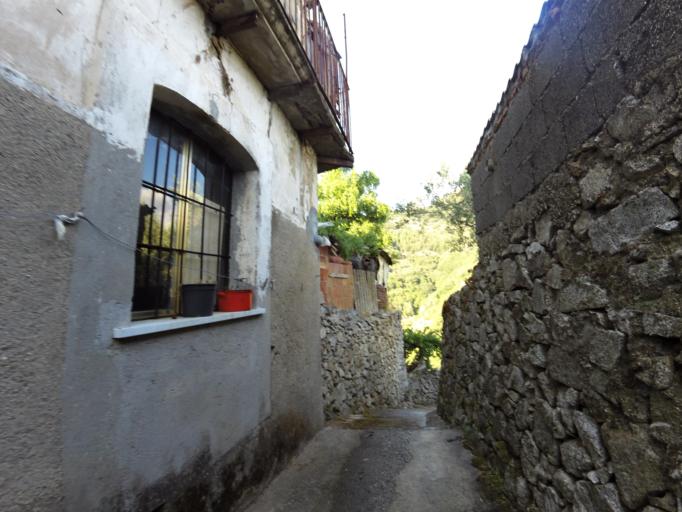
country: IT
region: Calabria
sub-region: Provincia di Vibo-Valentia
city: Nardodipace
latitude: 38.4452
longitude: 16.3484
